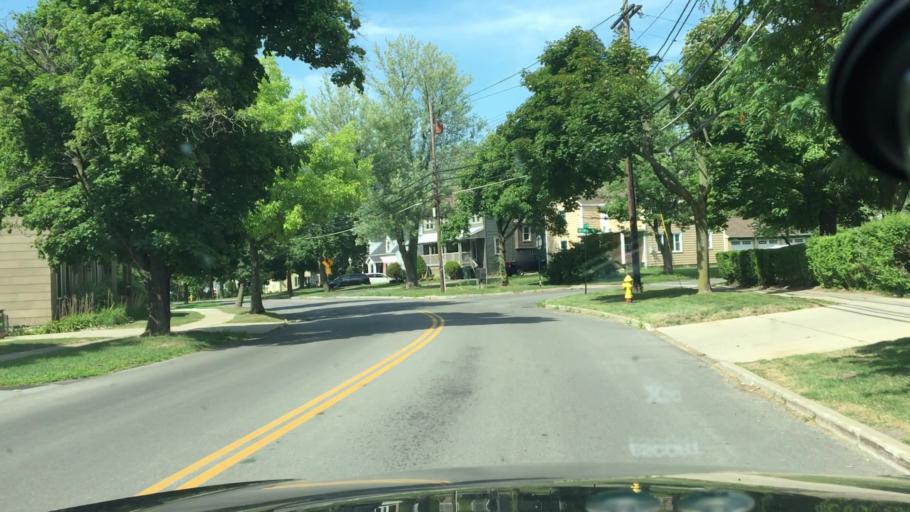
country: US
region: New York
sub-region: Erie County
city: Williamsville
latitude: 42.9676
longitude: -78.7433
